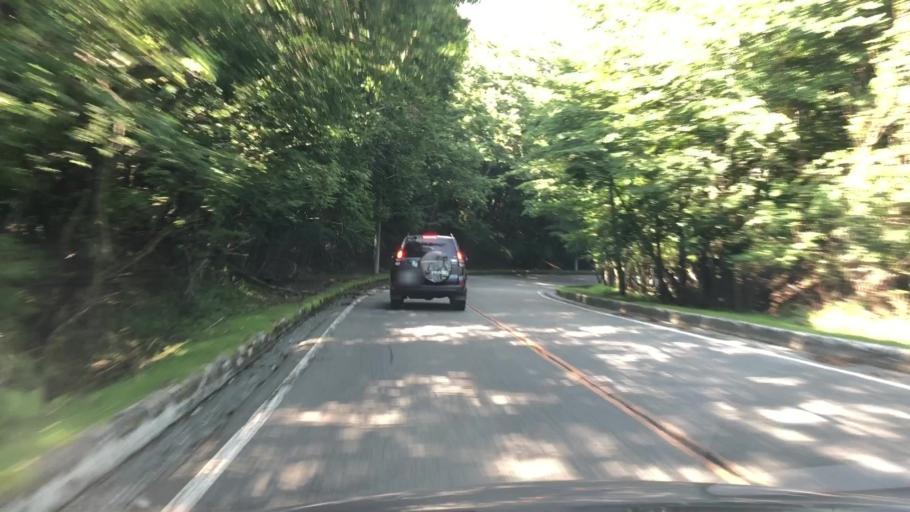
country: JP
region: Shizuoka
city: Gotemba
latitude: 35.3261
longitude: 138.7995
